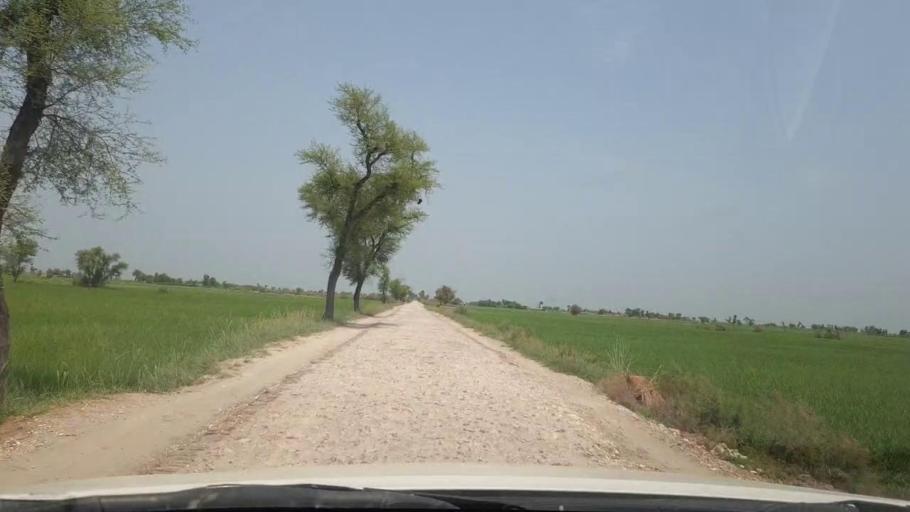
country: PK
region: Sindh
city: Rustam jo Goth
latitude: 28.0360
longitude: 68.8141
